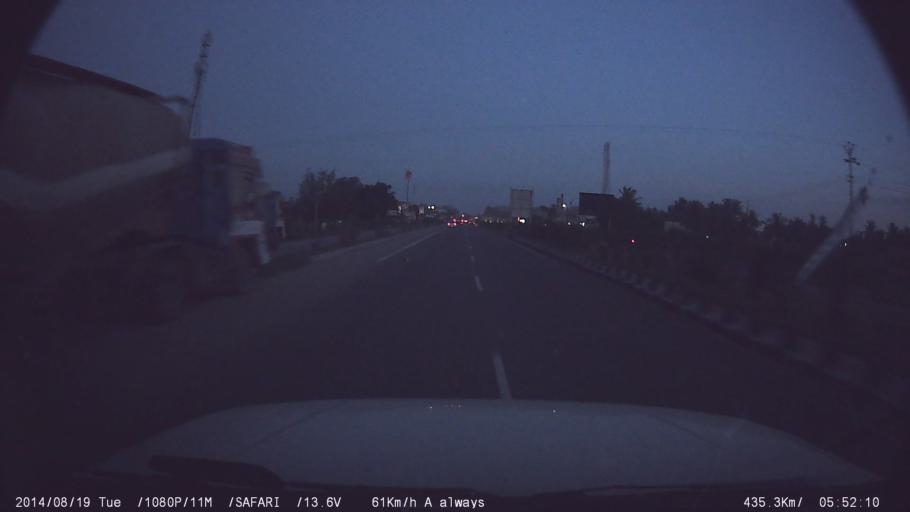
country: IN
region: Tamil Nadu
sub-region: Salem
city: Omalur
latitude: 11.7208
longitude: 78.0726
